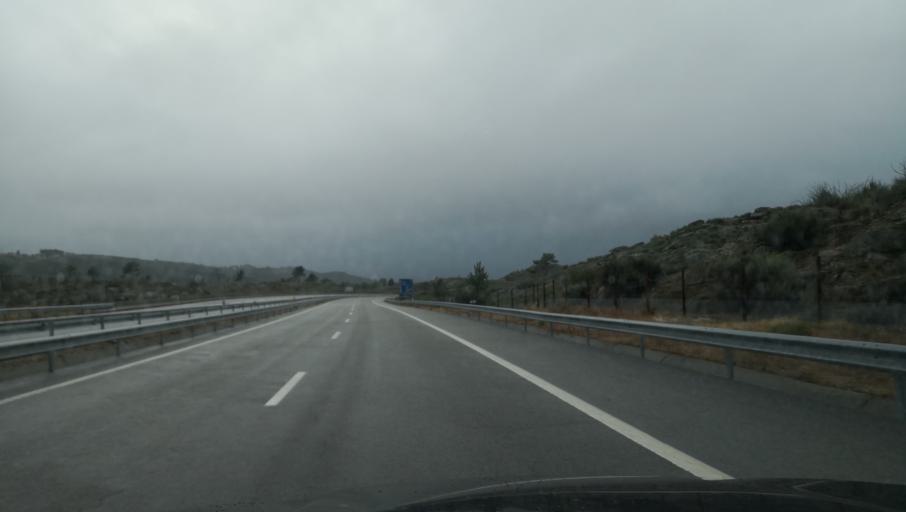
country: PT
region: Vila Real
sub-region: Vila Real
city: Vila Real
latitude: 41.3691
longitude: -7.6819
